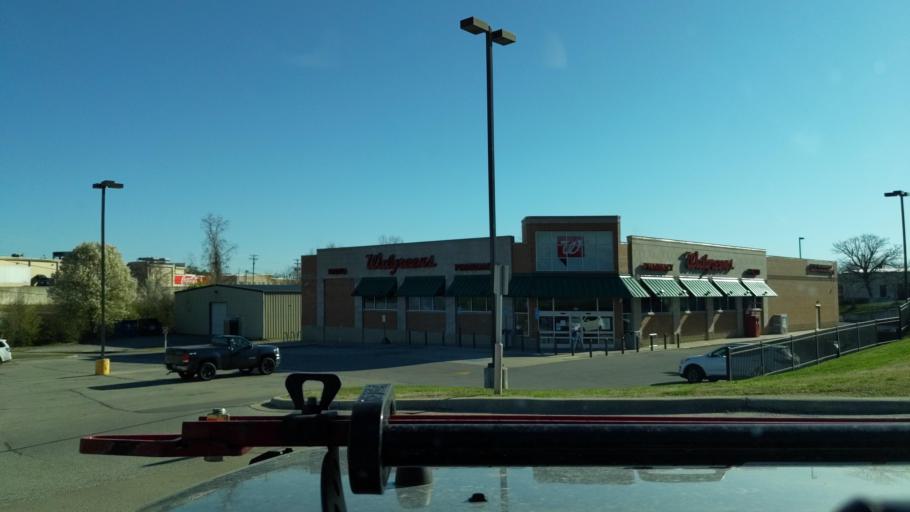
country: US
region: Missouri
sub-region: Taney County
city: Hollister
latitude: 36.6102
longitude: -93.2296
